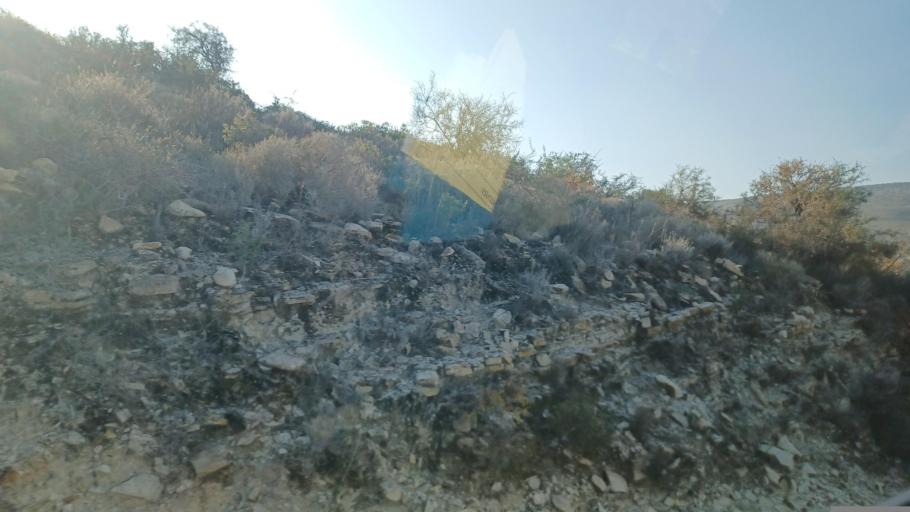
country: CY
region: Larnaka
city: Kofinou
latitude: 34.8317
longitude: 33.3041
